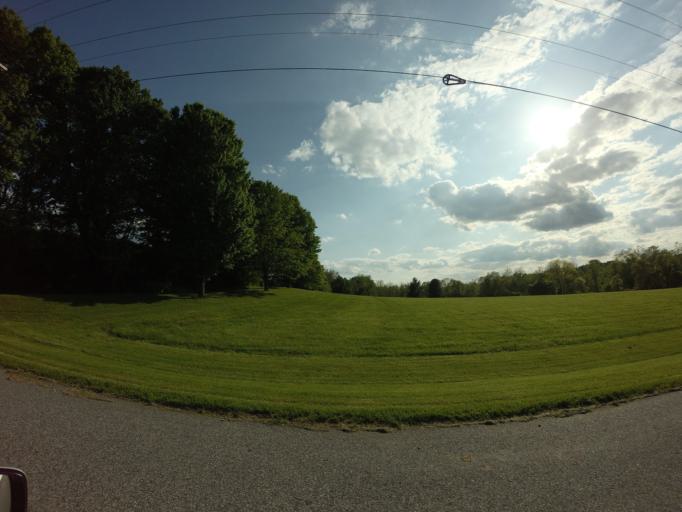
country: US
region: Maryland
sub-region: Baltimore County
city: Hunt Valley
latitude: 39.5272
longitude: -76.7232
